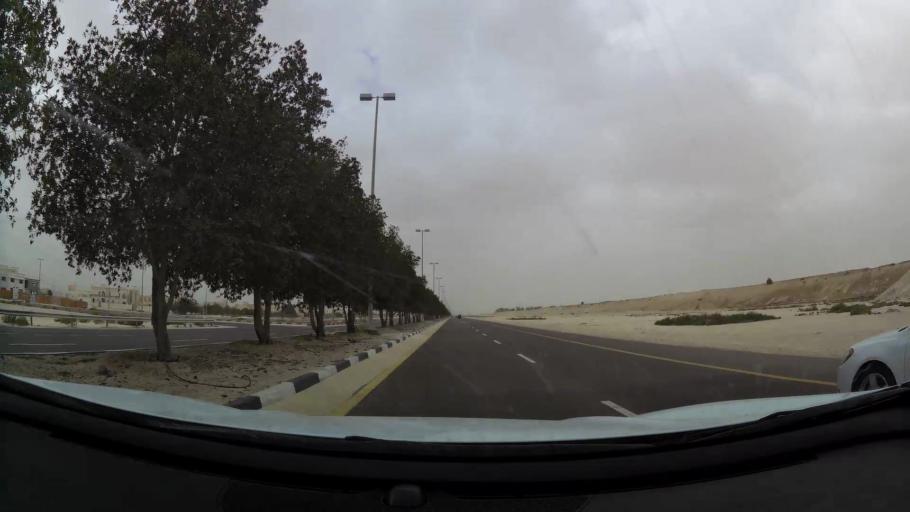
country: AE
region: Abu Dhabi
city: Abu Dhabi
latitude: 24.4002
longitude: 54.7103
